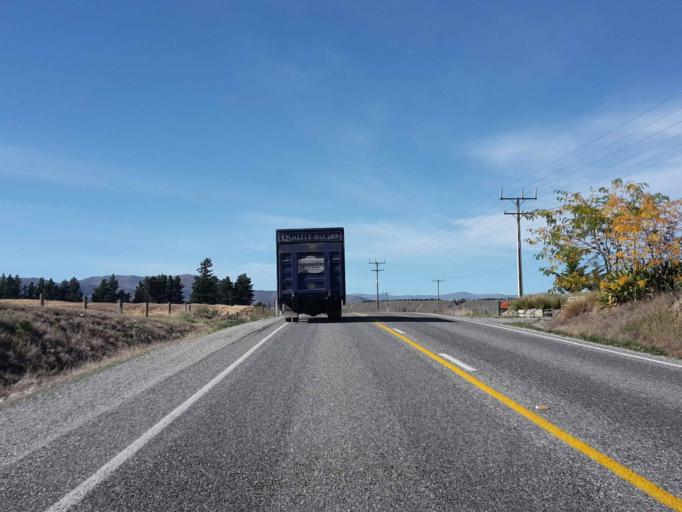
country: NZ
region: Otago
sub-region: Queenstown-Lakes District
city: Wanaka
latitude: -44.7176
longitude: 169.2179
